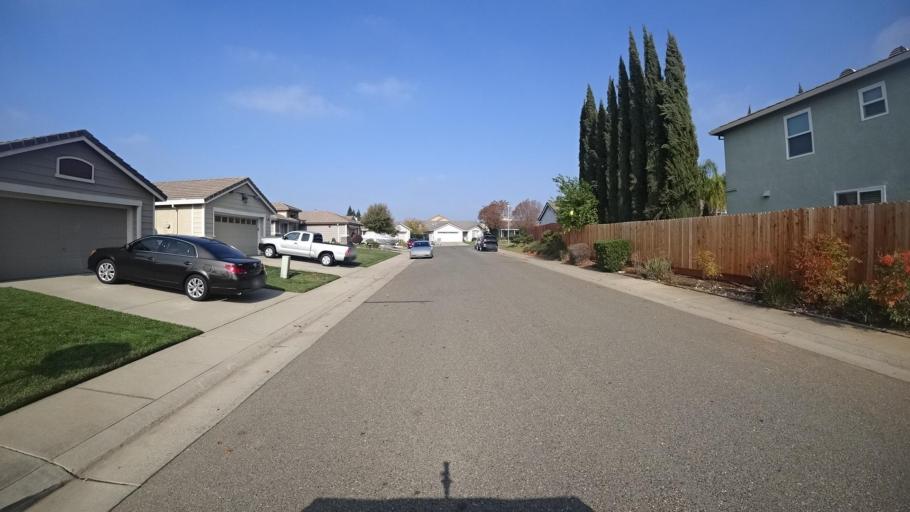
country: US
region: California
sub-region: Sacramento County
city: Vineyard
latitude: 38.4426
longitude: -121.3652
